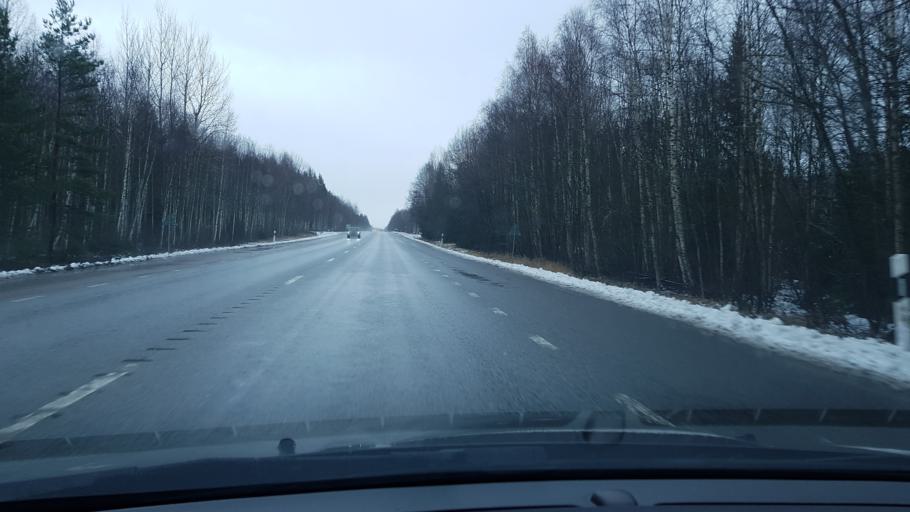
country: SE
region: Uppsala
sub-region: Heby Kommun
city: Morgongava
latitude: 59.8959
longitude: 17.1178
